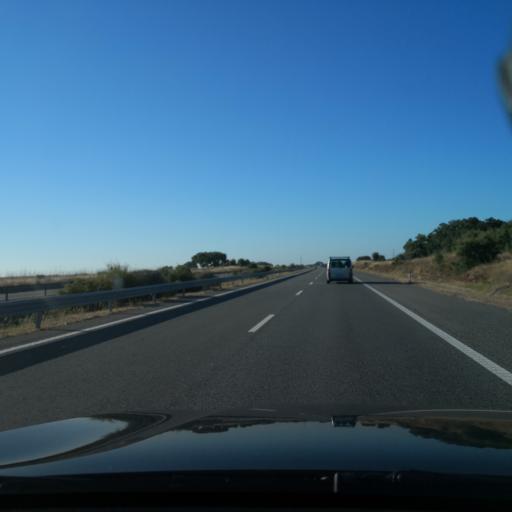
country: PT
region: Setubal
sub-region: Grandola
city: Grandola
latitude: 38.1825
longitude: -8.5048
